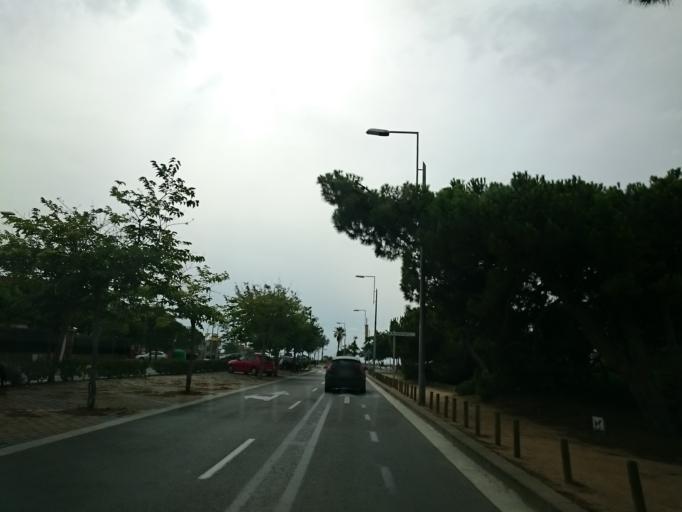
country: ES
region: Catalonia
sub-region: Provincia de Barcelona
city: Castelldefels
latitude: 41.2656
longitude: 1.9842
